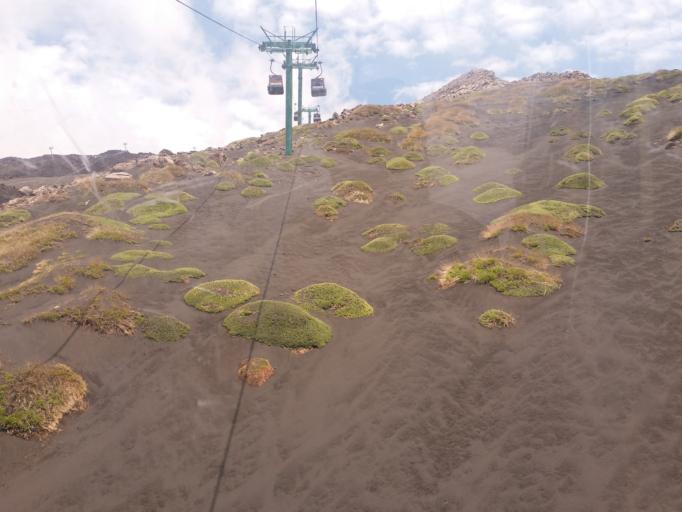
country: IT
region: Sicily
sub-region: Catania
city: Ragalna
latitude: 37.7126
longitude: 14.9997
